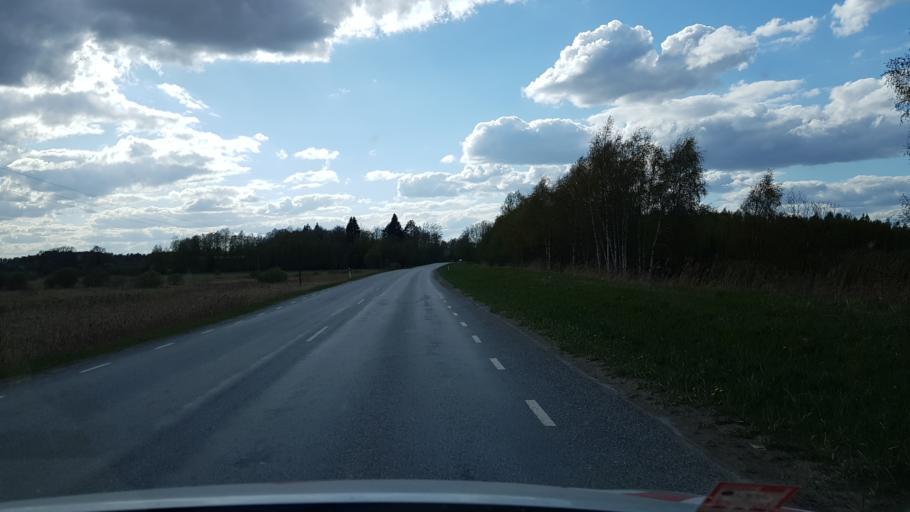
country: EE
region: Tartu
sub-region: UElenurme vald
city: Ulenurme
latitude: 58.3279
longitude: 26.7526
